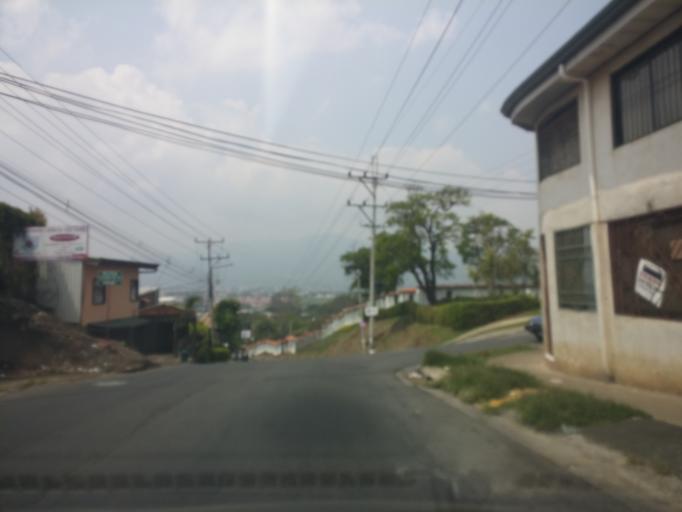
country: CR
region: Heredia
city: San Francisco
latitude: 9.9861
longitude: -84.1209
